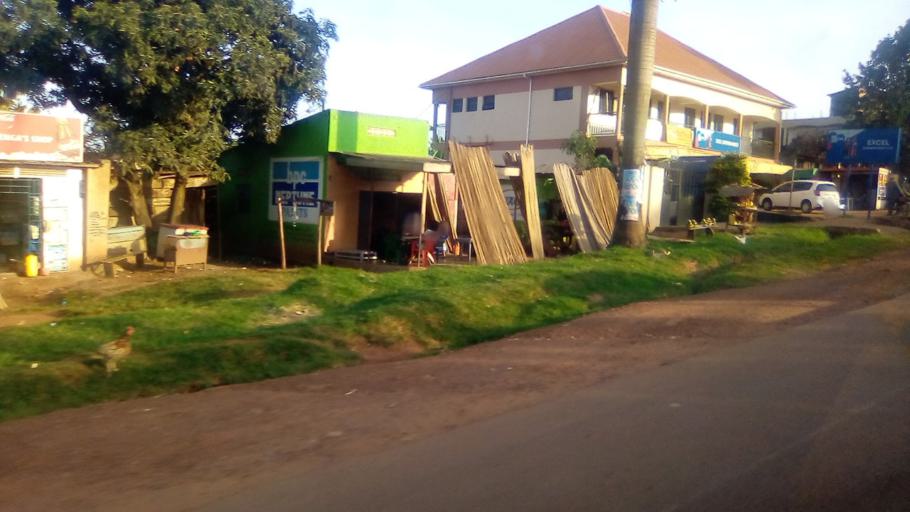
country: UG
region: Central Region
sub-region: Wakiso District
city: Kajansi
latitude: 0.1853
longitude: 32.5387
